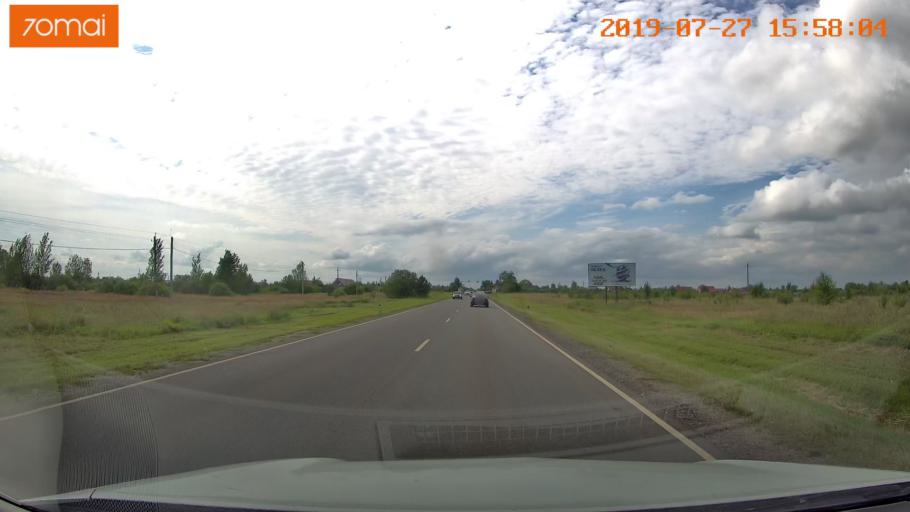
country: RU
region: Kaliningrad
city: Chernyakhovsk
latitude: 54.6255
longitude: 21.8713
